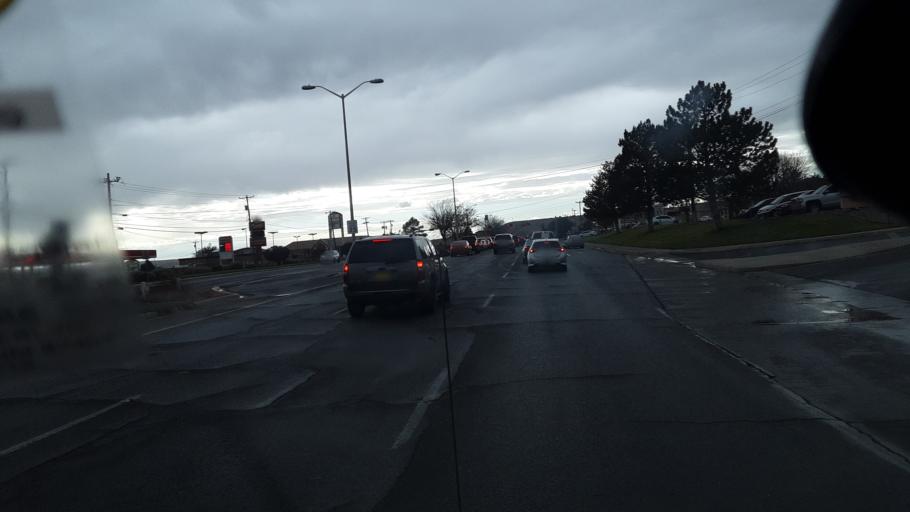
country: US
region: New Mexico
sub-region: San Juan County
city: Flora Vista
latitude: 36.7678
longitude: -108.1468
